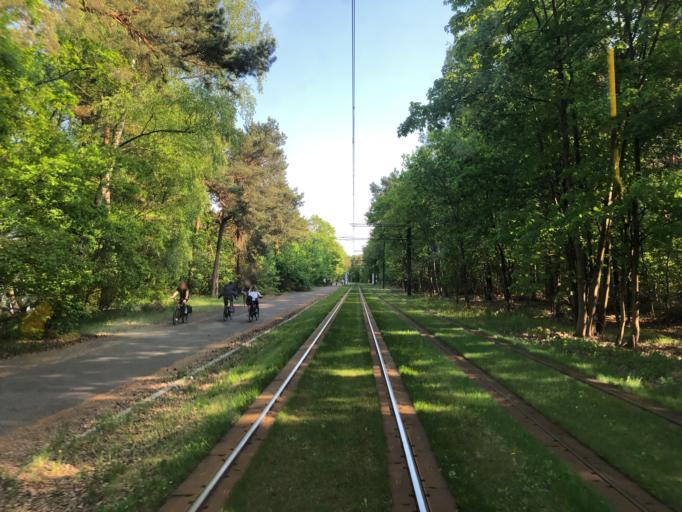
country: DE
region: Brandenburg
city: Zeuthen
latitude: 52.4026
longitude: 13.6239
